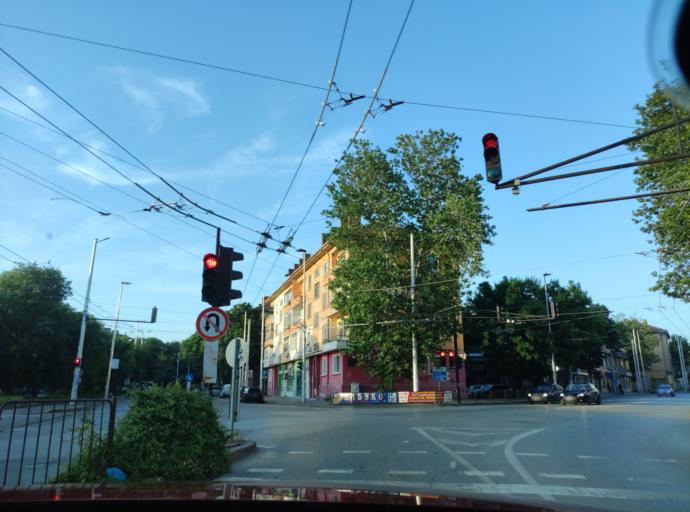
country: BG
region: Pleven
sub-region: Obshtina Pleven
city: Pleven
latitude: 43.4174
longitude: 24.6133
